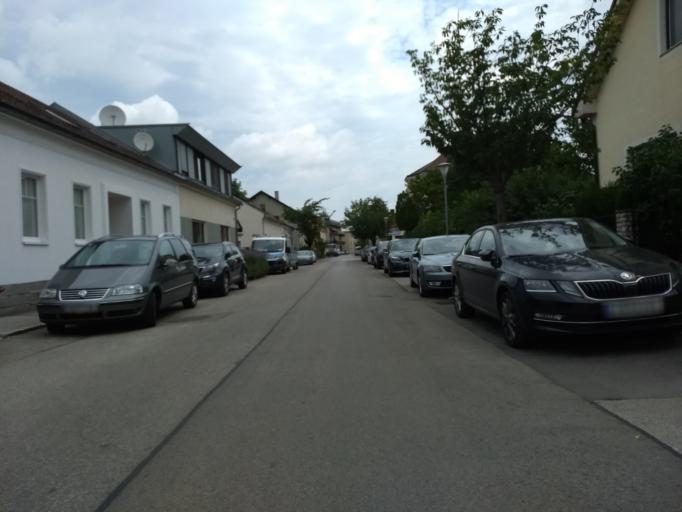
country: AT
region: Lower Austria
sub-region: Politischer Bezirk Modling
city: Guntramsdorf
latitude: 48.0447
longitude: 16.3076
